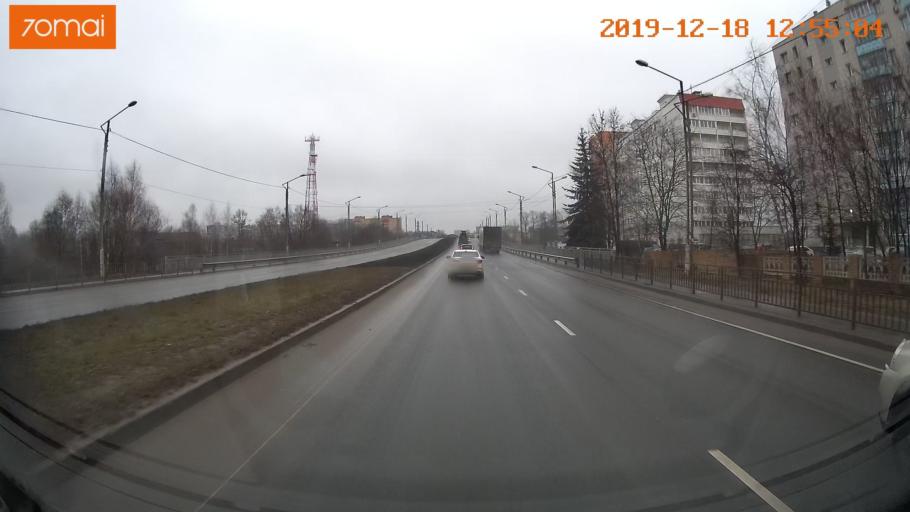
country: RU
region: Moskovskaya
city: Klin
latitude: 56.3283
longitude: 36.7075
